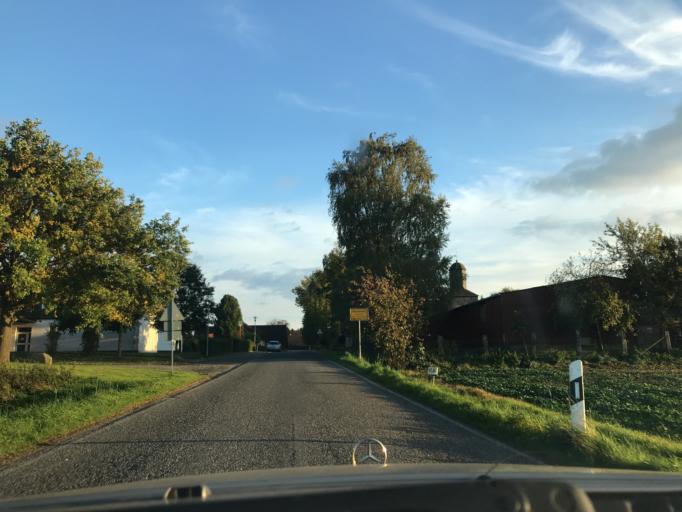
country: DE
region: Hesse
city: Witzenhausen
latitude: 51.4060
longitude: 9.8596
